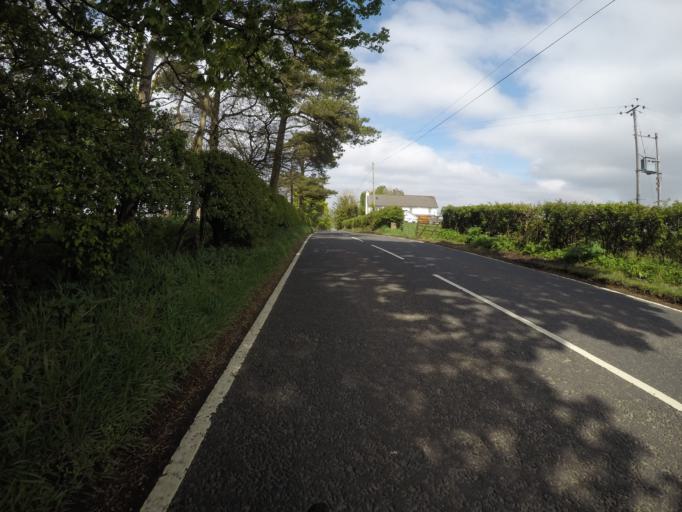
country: GB
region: Scotland
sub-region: East Renfrewshire
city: Newton Mearns
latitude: 55.7765
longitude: -4.3614
